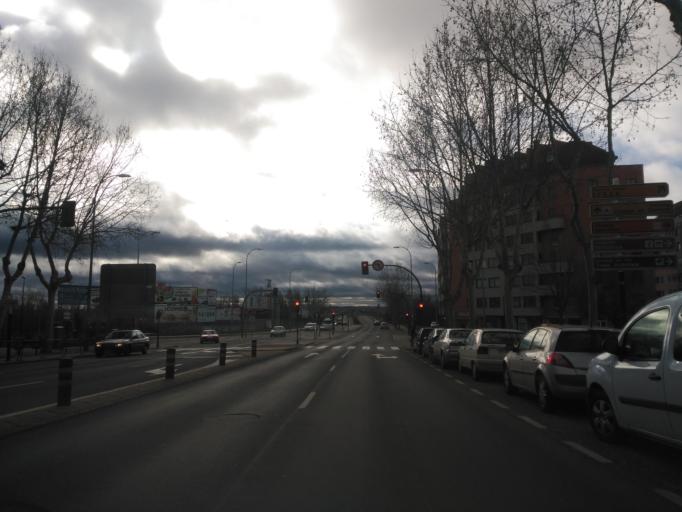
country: ES
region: Castille and Leon
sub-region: Provincia de Zamora
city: Zamora
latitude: 41.5059
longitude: -5.7324
